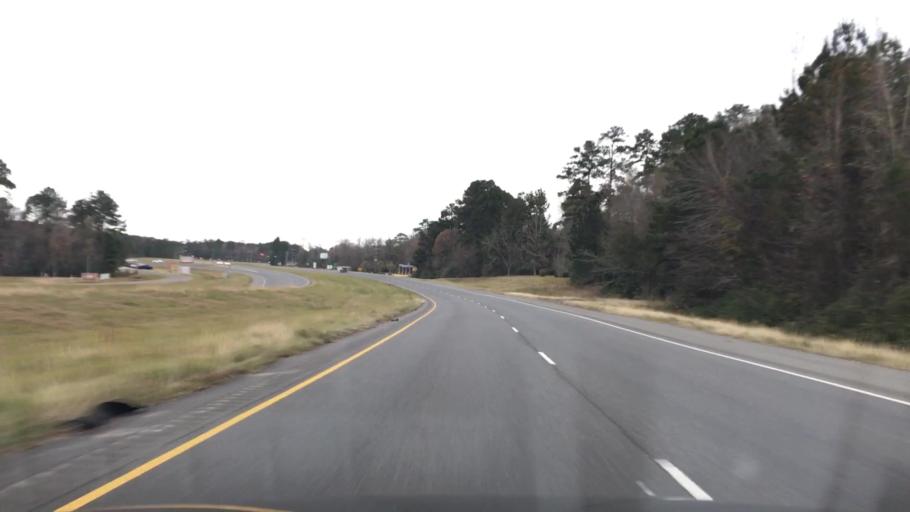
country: US
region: Louisiana
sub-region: Vernon Parish
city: New Llano
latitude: 31.0708
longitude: -93.2742
